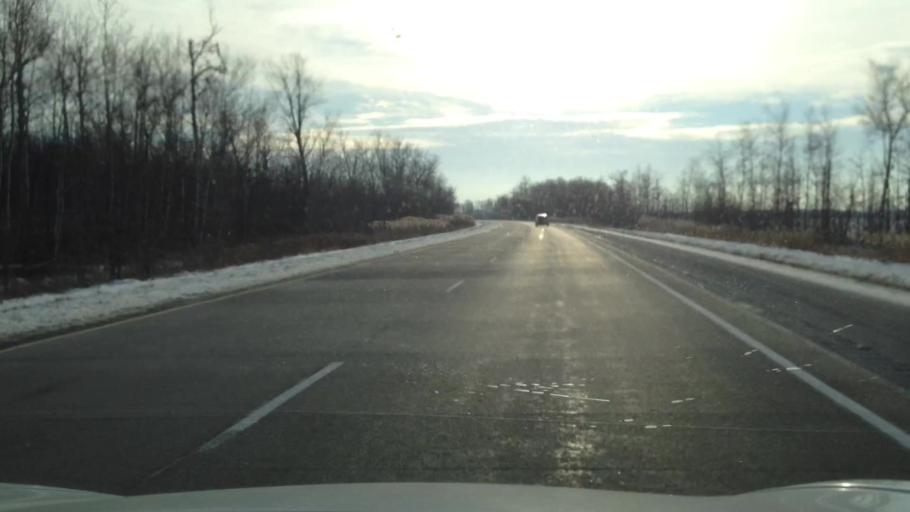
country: CA
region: Ontario
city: Hawkesbury
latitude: 45.4249
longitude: -74.7615
